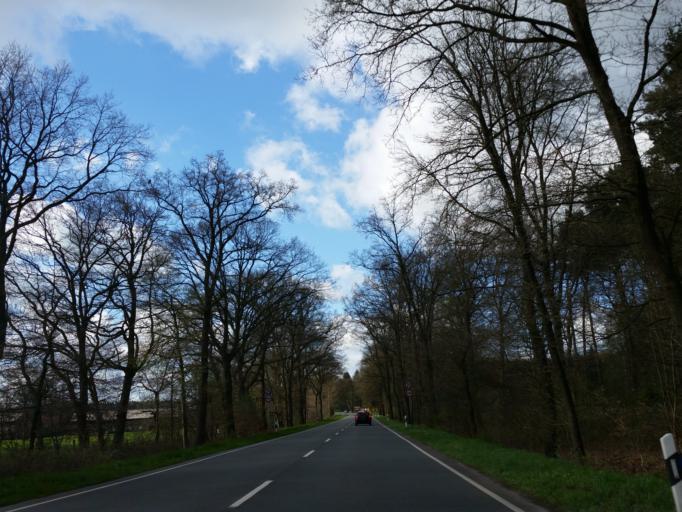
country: DE
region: Lower Saxony
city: Ahausen
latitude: 53.0155
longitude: 9.2772
